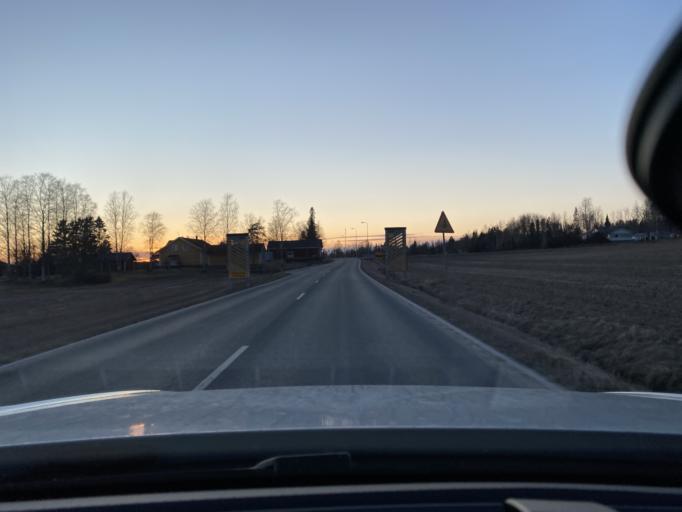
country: FI
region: Pirkanmaa
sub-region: Lounais-Pirkanmaa
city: Punkalaidun
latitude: 61.1065
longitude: 23.1374
